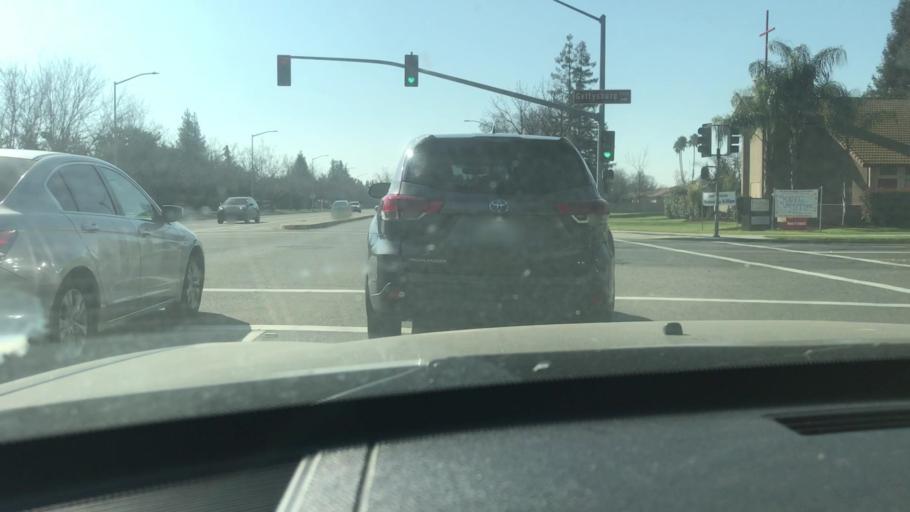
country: US
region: California
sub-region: Fresno County
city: Tarpey Village
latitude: 36.8013
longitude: -119.6640
